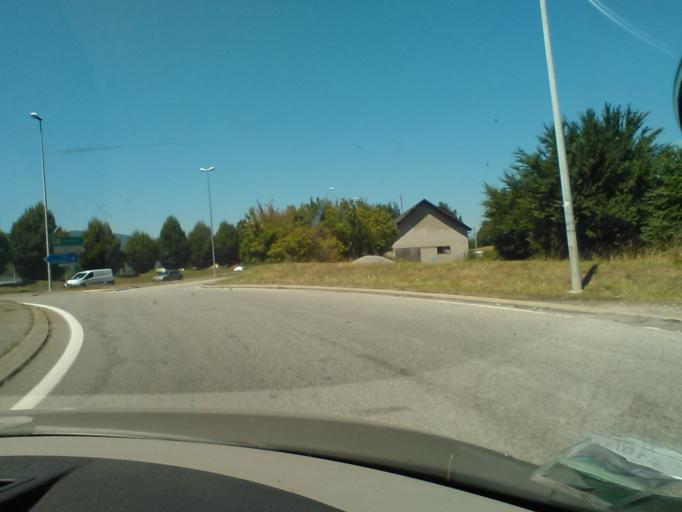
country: FR
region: Rhone-Alpes
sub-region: Departement de la Savoie
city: Les Marches
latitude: 45.5133
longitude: 6.0092
